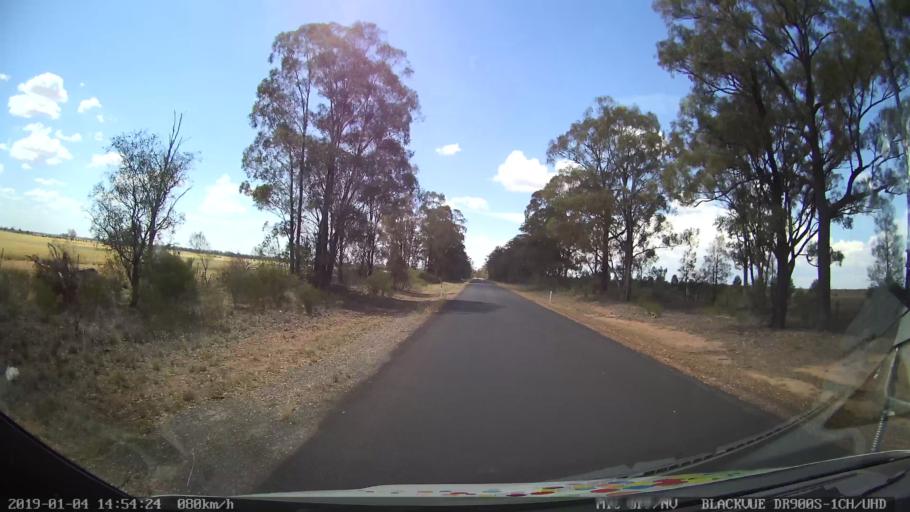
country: AU
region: New South Wales
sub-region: Dubbo Municipality
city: Dubbo
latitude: -31.9913
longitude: 148.6538
